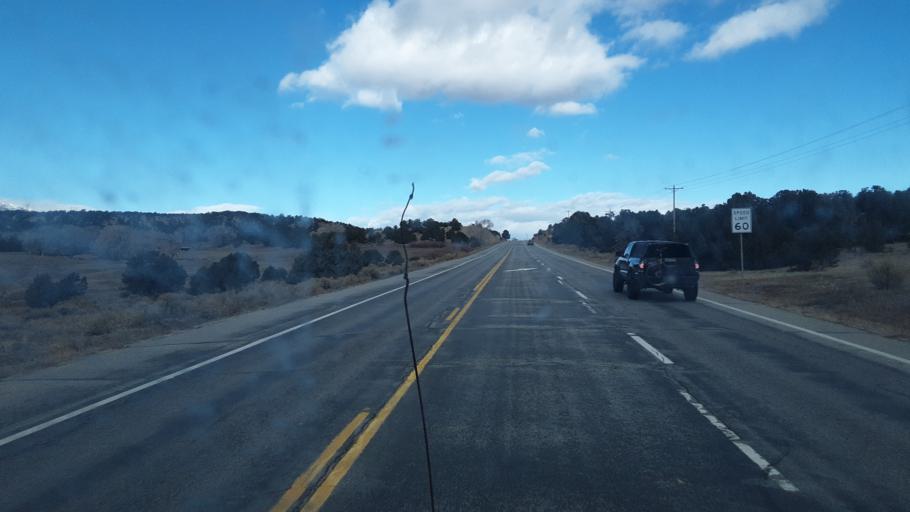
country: US
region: Colorado
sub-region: Chaffee County
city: Salida
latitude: 38.6685
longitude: -106.0900
